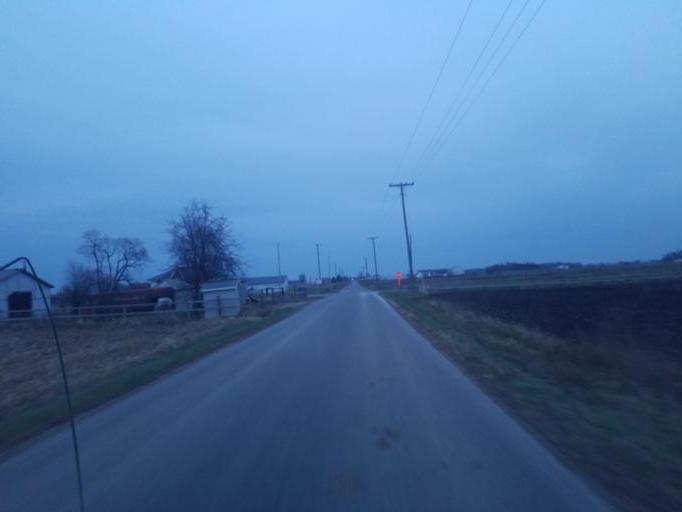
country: US
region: Indiana
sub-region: Adams County
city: Berne
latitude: 40.7312
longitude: -84.8993
